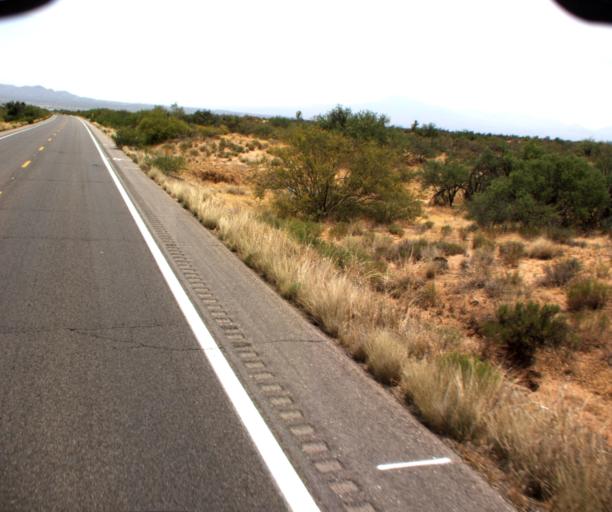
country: US
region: Arizona
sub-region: Gila County
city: Peridot
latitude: 33.3111
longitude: -110.5067
